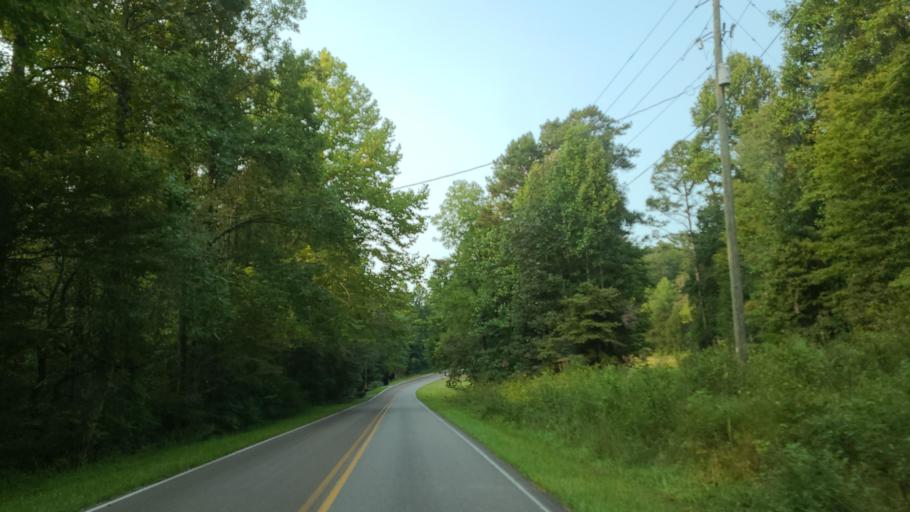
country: US
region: Georgia
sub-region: Gilmer County
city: Ellijay
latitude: 34.7842
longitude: -84.4256
